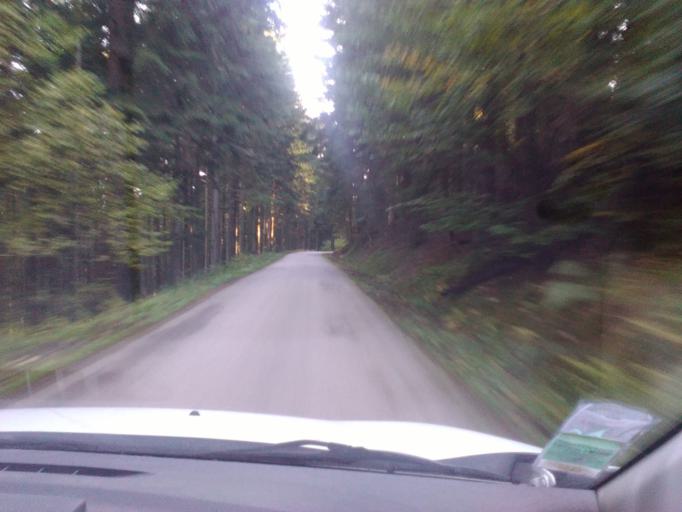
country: FR
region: Lorraine
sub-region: Departement des Vosges
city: Taintrux
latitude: 48.2295
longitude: 6.8759
